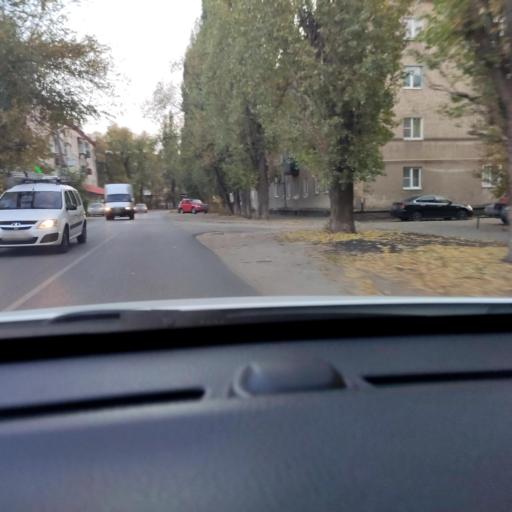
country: RU
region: Voronezj
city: Voronezh
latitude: 51.6622
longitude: 39.2798
